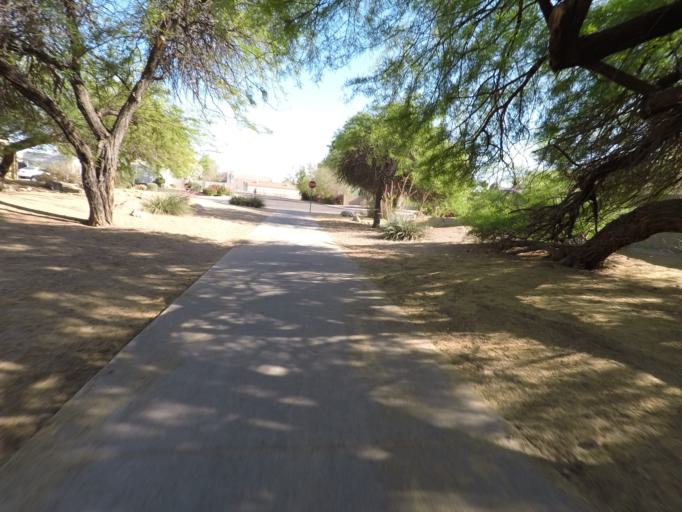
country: US
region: Arizona
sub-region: Maricopa County
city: Guadalupe
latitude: 33.3562
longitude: -111.9199
